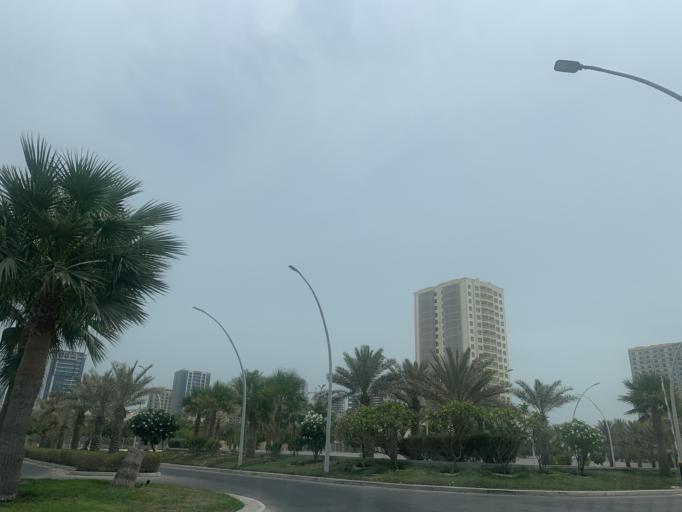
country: BH
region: Muharraq
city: Al Hadd
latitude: 26.2907
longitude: 50.6608
